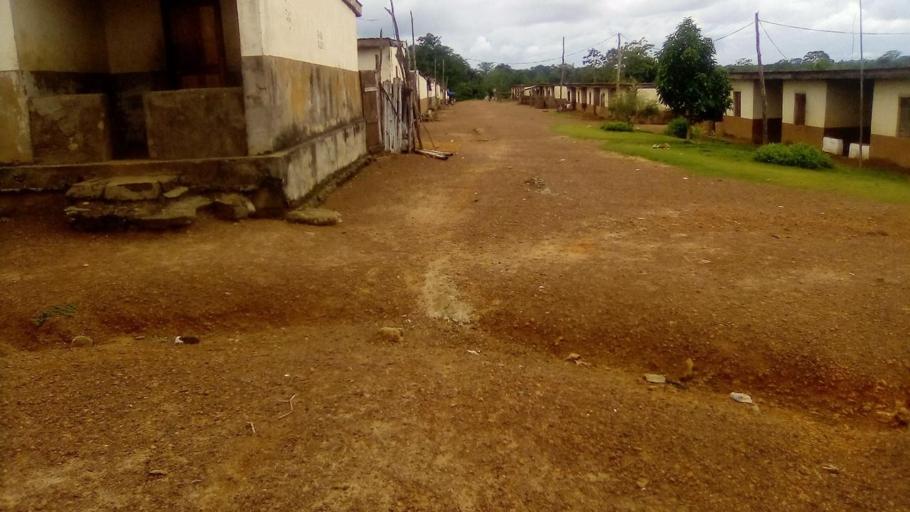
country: SL
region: Southern Province
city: Pujehun
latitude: 7.3709
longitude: -11.7264
